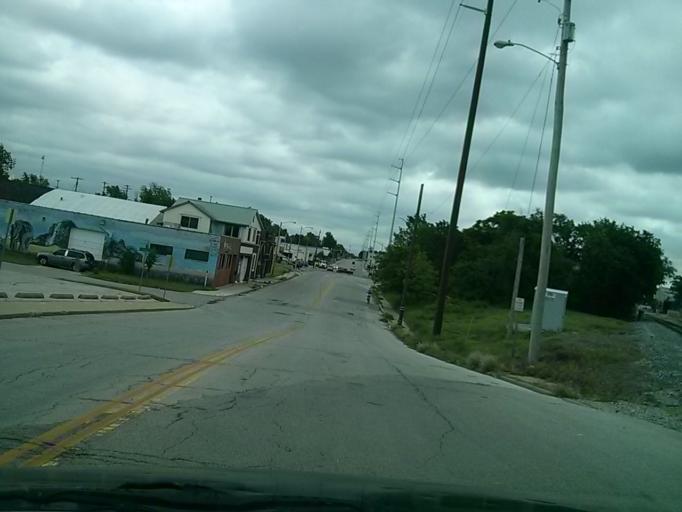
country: US
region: Oklahoma
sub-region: Tulsa County
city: Tulsa
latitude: 36.1567
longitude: -95.9779
